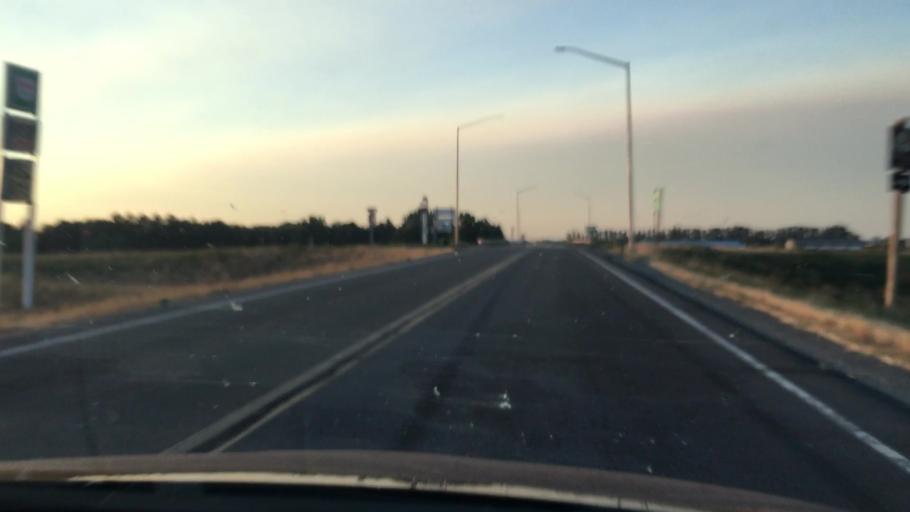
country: US
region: Idaho
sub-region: Minidoka County
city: Rupert
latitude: 42.5672
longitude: -113.6237
